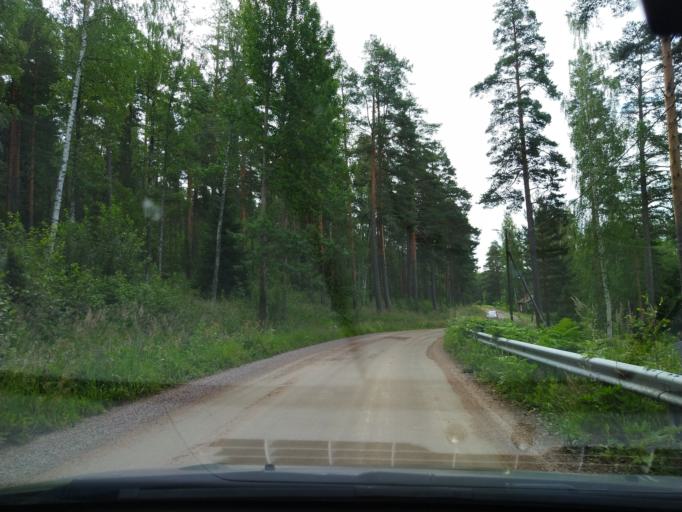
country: FI
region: Kymenlaakso
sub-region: Kouvola
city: Jaala
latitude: 61.0607
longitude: 26.6462
